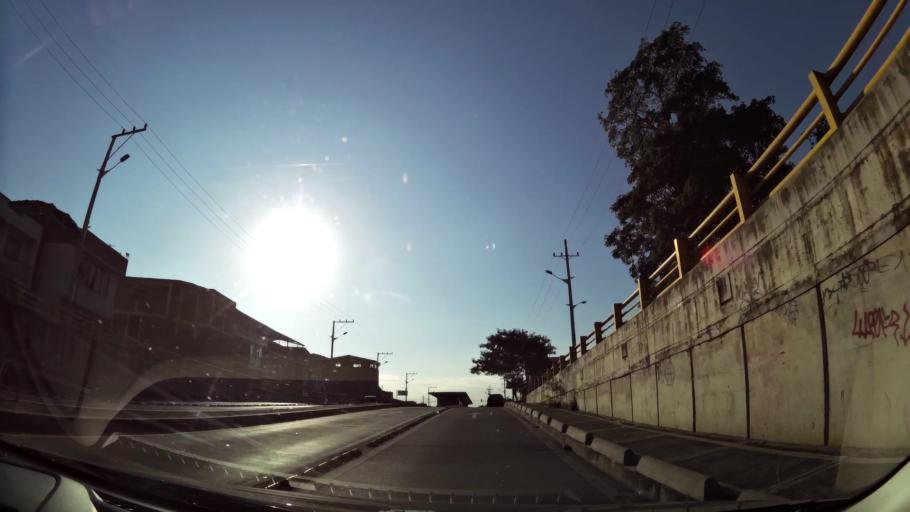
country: CO
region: Valle del Cauca
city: Cali
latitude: 3.4379
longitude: -76.5184
